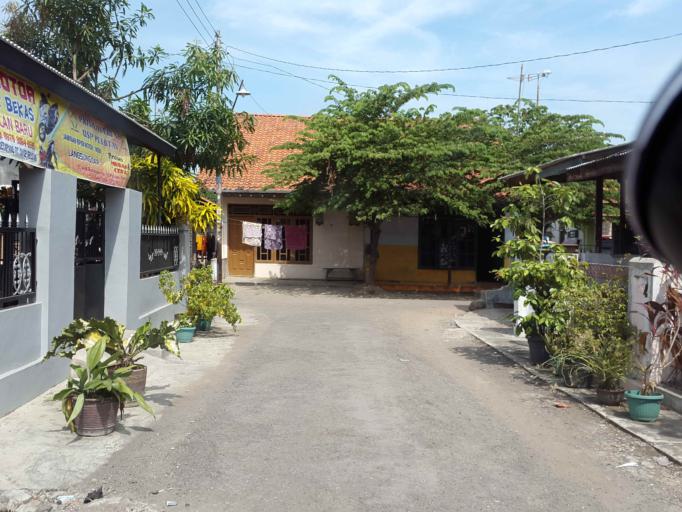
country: ID
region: Central Java
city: Pemalang
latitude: -6.8854
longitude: 109.3781
